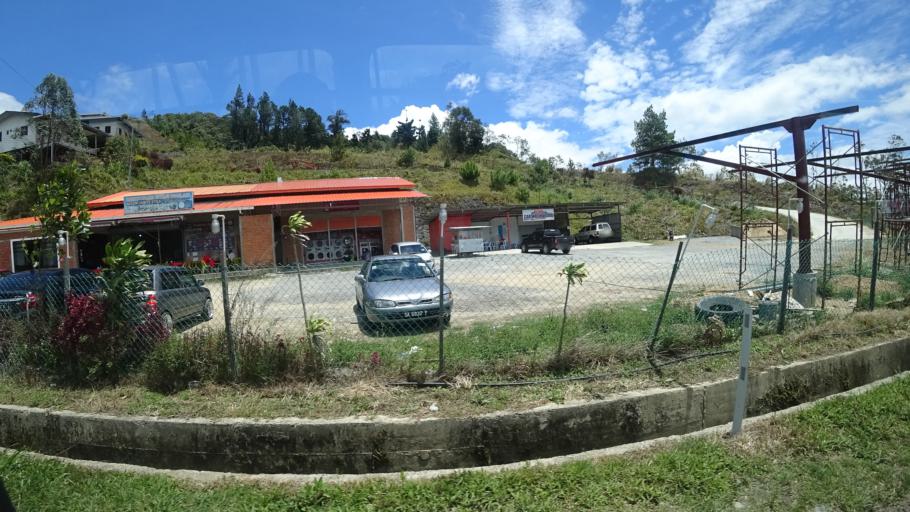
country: MY
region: Sabah
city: Ranau
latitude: 5.9812
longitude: 116.5618
